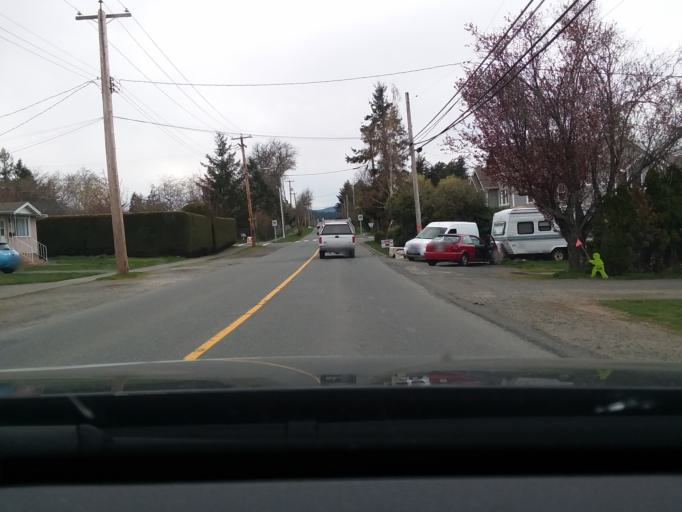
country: CA
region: British Columbia
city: Victoria
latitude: 48.4792
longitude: -123.4160
